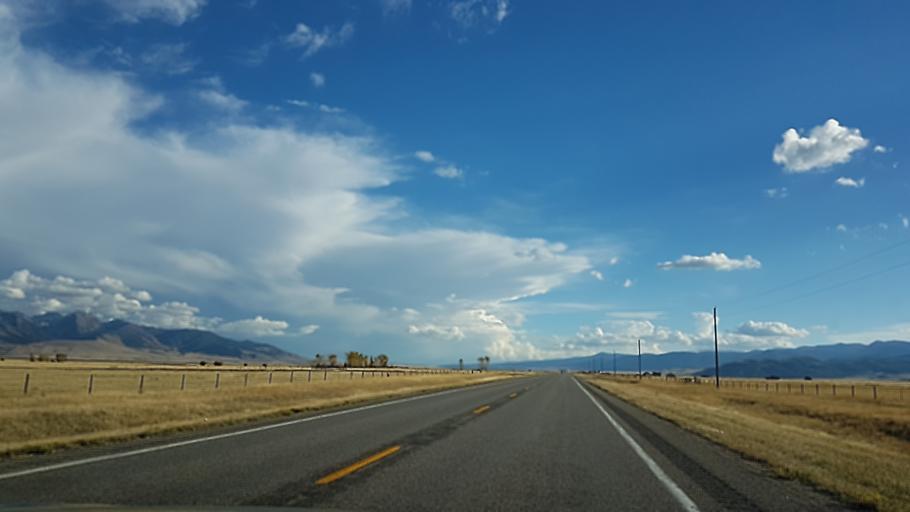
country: US
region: Montana
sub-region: Madison County
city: Virginia City
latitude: 45.1910
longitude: -111.6789
